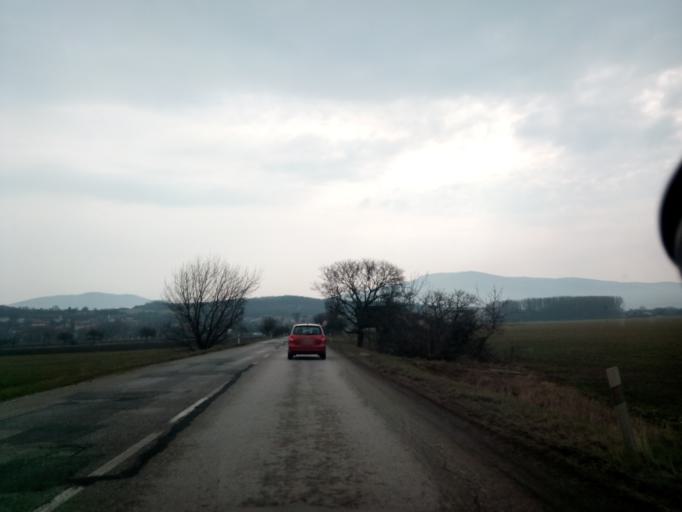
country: SK
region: Kosicky
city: Kosice
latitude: 48.6606
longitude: 21.3457
